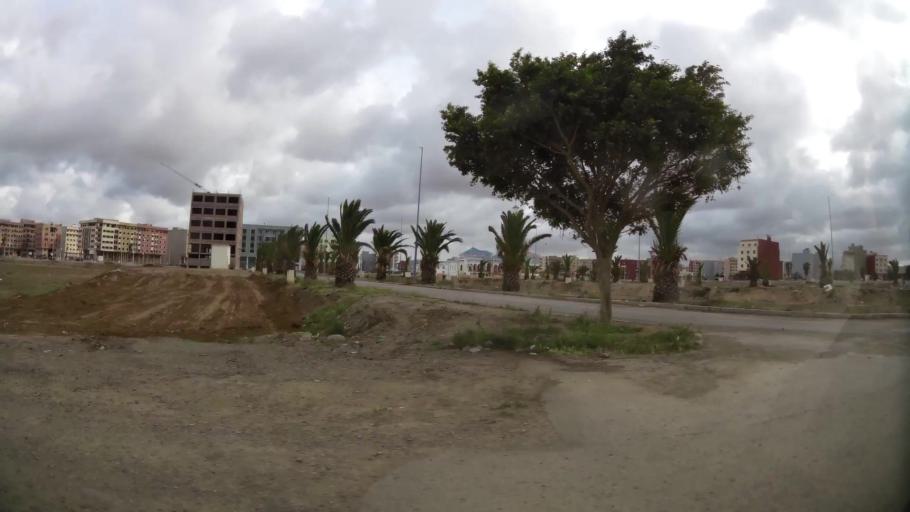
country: MA
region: Oriental
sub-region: Nador
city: Nador
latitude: 35.1558
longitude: -2.9160
